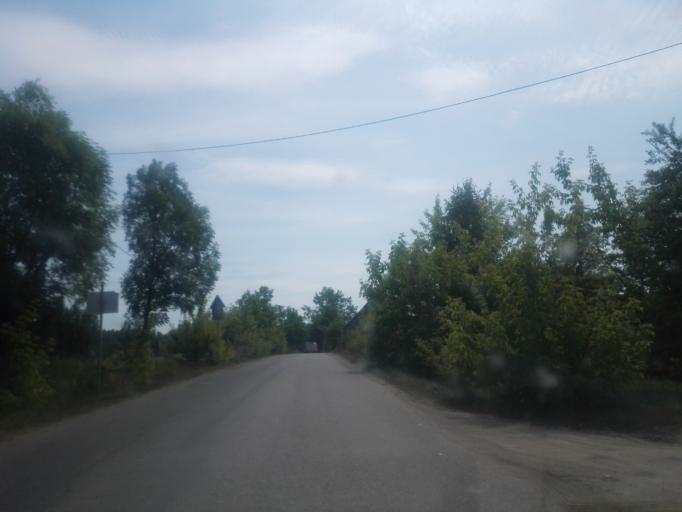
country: PL
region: Podlasie
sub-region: Powiat sejnenski
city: Krasnopol
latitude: 54.0910
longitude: 23.1452
